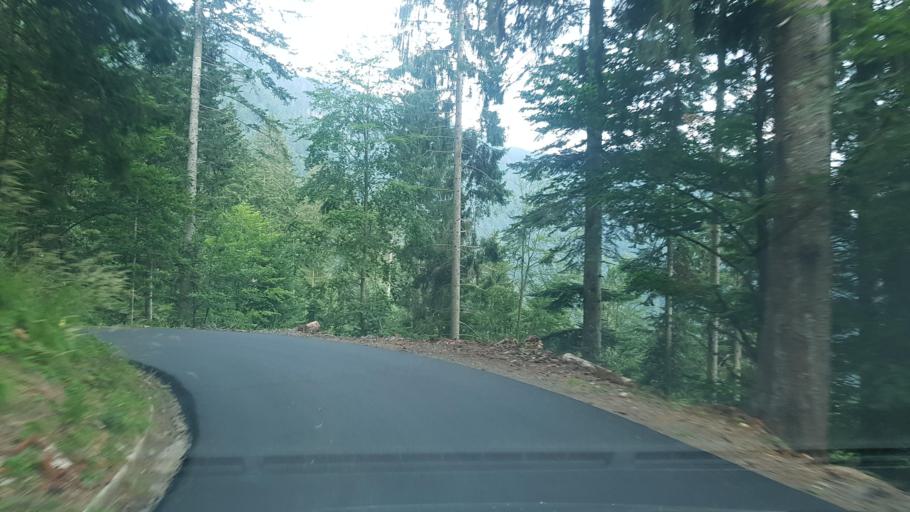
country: IT
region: Friuli Venezia Giulia
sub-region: Provincia di Udine
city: Paularo
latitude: 46.5629
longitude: 13.1179
